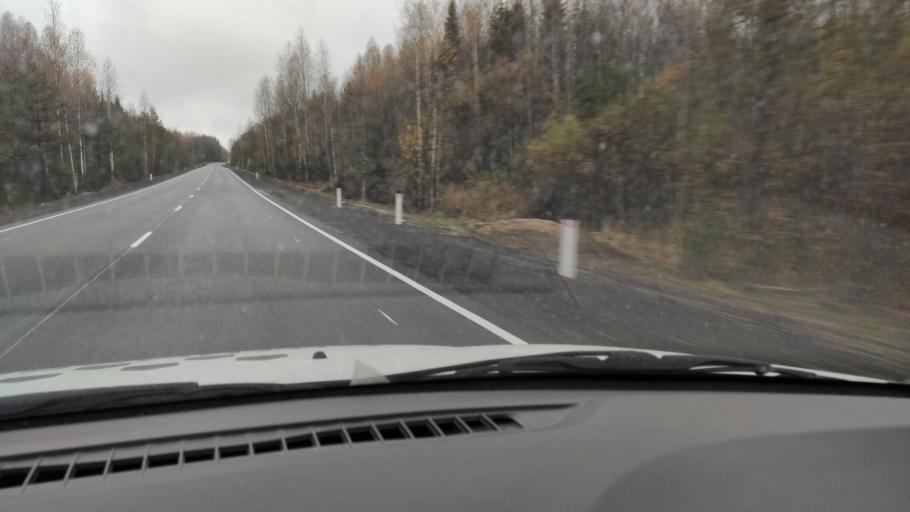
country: RU
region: Kirov
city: Chernaya Kholunitsa
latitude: 58.8768
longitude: 51.4739
